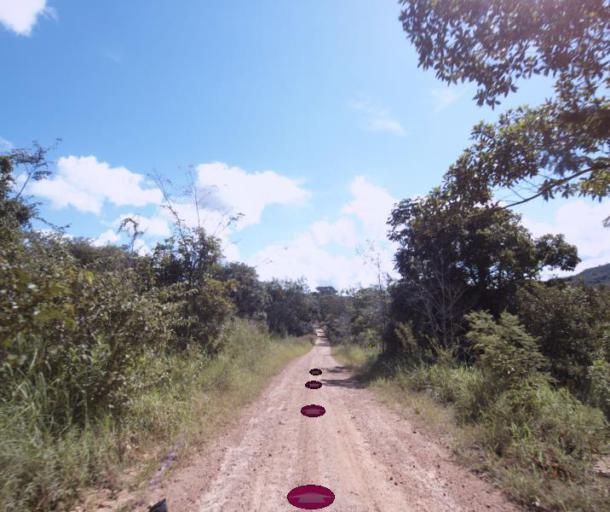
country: BR
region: Goias
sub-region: Pirenopolis
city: Pirenopolis
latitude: -15.7744
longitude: -49.0215
